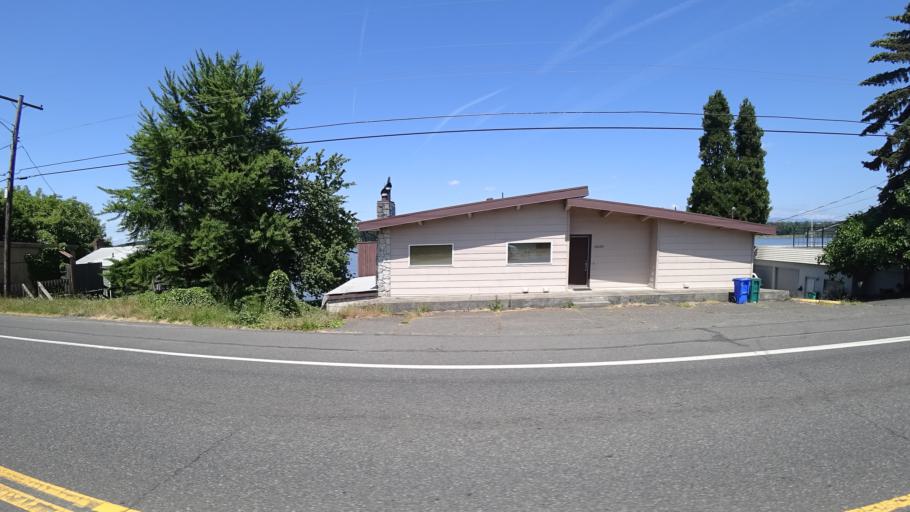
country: US
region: Washington
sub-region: Clark County
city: Mill Plain
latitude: 45.5653
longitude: -122.5223
